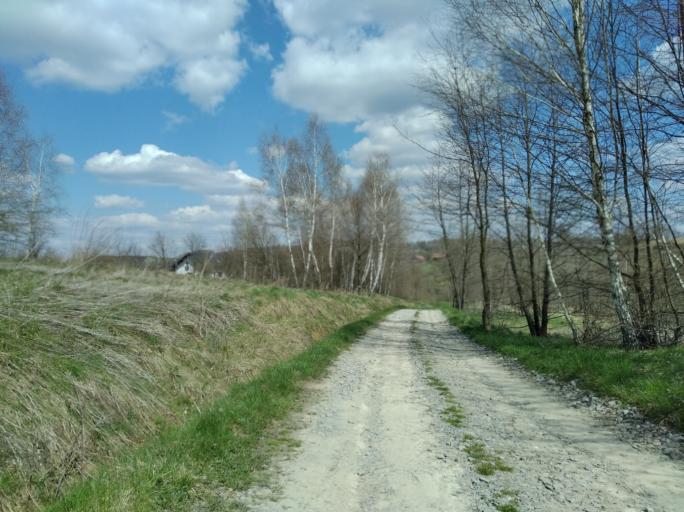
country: PL
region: Subcarpathian Voivodeship
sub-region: Powiat strzyzowski
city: Wysoka Strzyzowska
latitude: 49.8461
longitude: 21.7595
